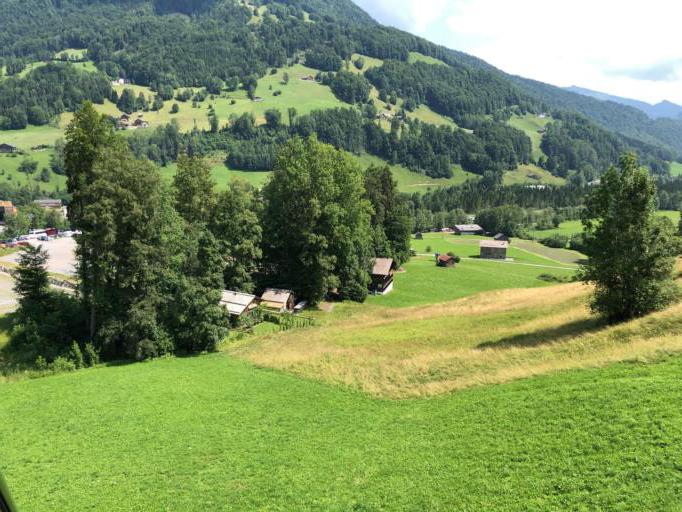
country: AT
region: Vorarlberg
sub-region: Politischer Bezirk Bregenz
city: Reuthe
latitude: 47.3424
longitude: 9.8882
